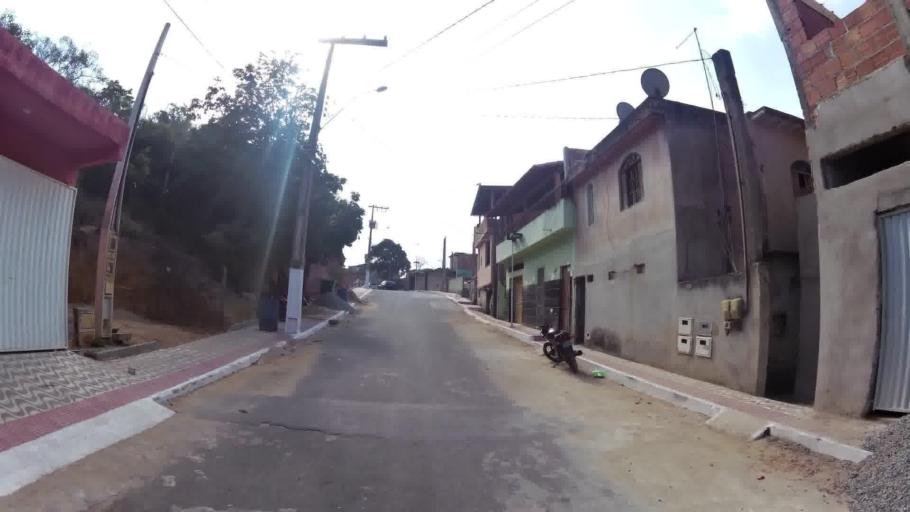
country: BR
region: Espirito Santo
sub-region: Itapemirim
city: Itapemirim
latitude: -21.0063
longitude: -40.8306
